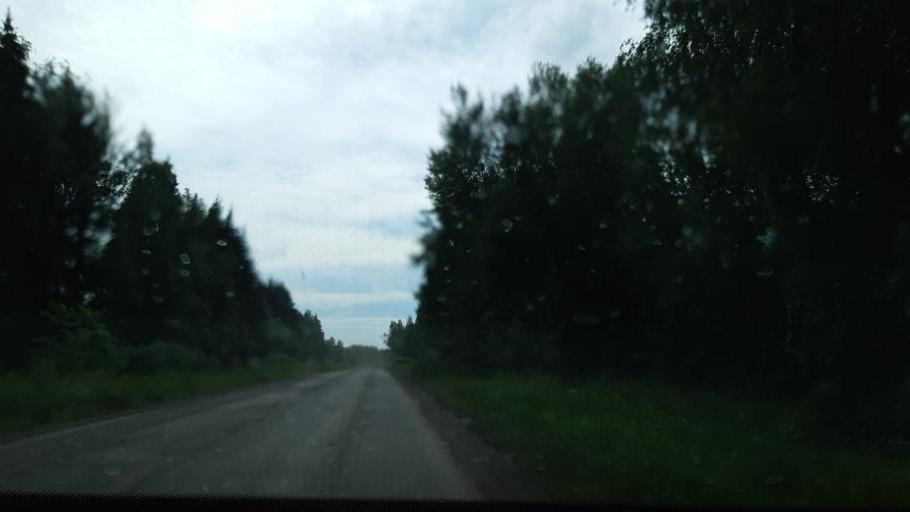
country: RU
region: Moskovskaya
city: Vereya
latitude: 55.3183
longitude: 36.1299
